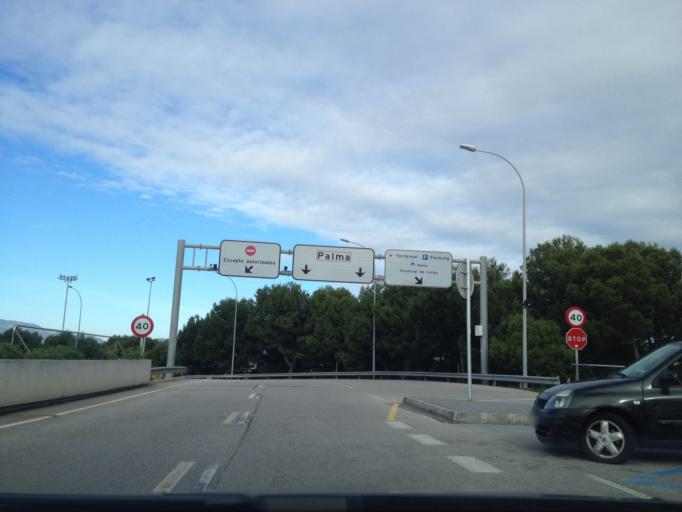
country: ES
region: Balearic Islands
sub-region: Illes Balears
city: s'Arenal
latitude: 39.5486
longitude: 2.7295
